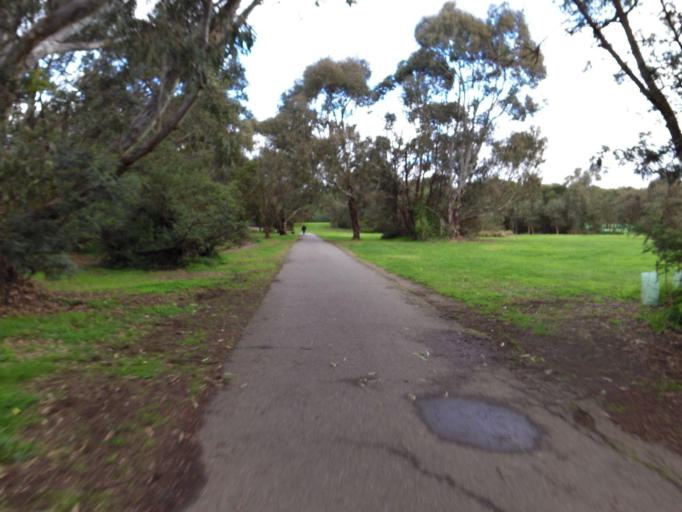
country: AU
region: Victoria
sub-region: Greater Geelong
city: Hamlyn Heights
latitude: -38.1449
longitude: 144.3132
